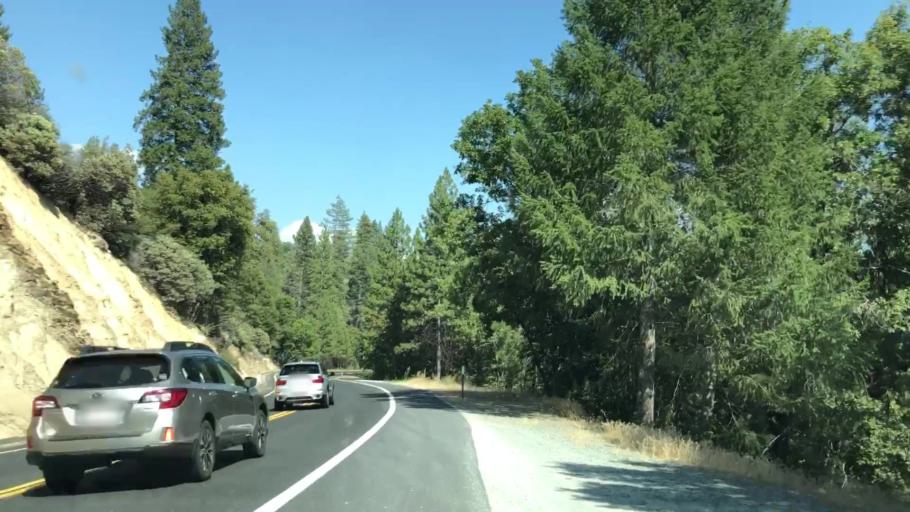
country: US
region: California
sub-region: Mariposa County
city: Midpines
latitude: 37.8161
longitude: -119.9447
